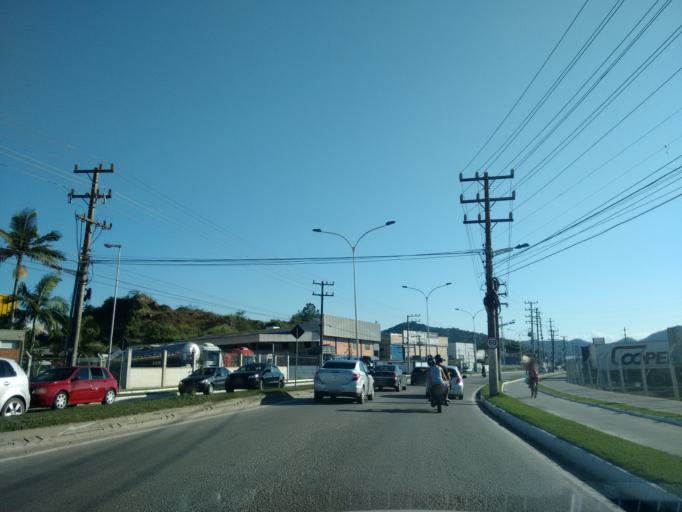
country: BR
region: Santa Catarina
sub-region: Itajai
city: Itajai
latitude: -26.8906
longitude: -48.7114
